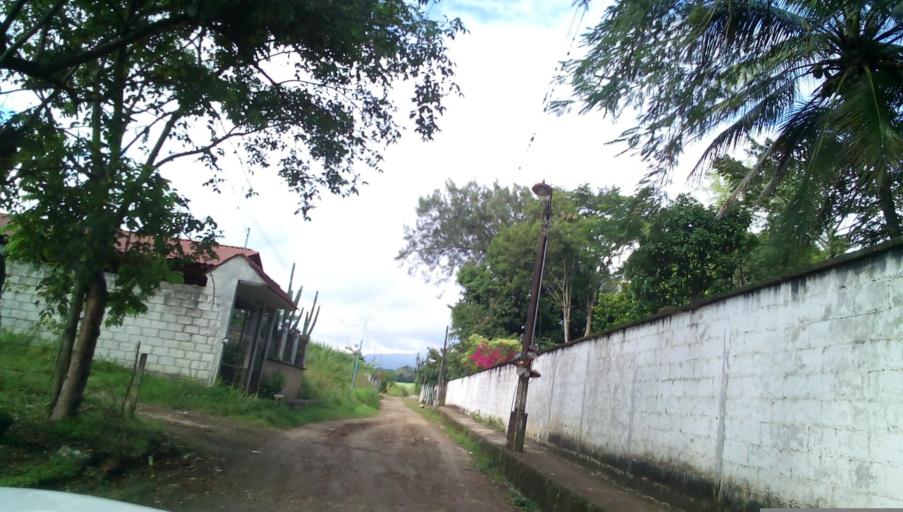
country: MX
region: Veracruz
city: Amatlan de los Reyes
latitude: 18.8249
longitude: -96.9216
